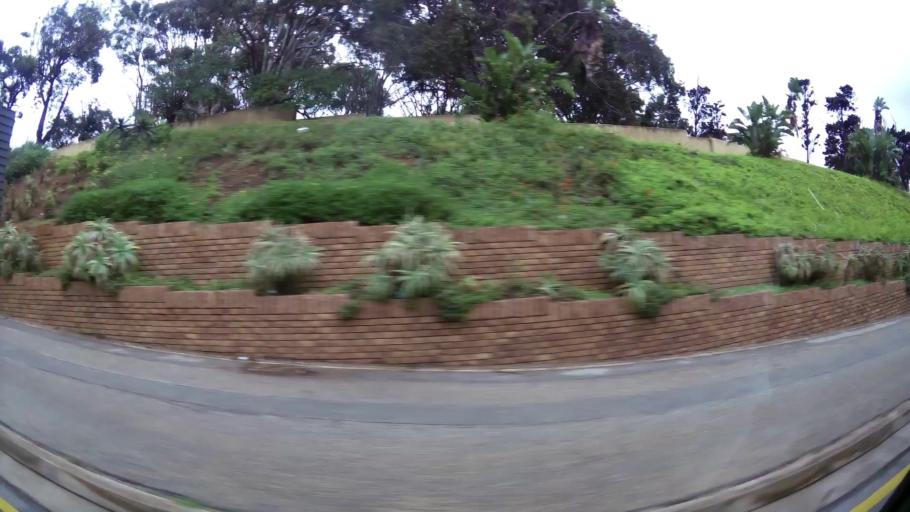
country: ZA
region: Eastern Cape
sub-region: Nelson Mandela Bay Metropolitan Municipality
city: Port Elizabeth
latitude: -33.9658
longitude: 25.6267
